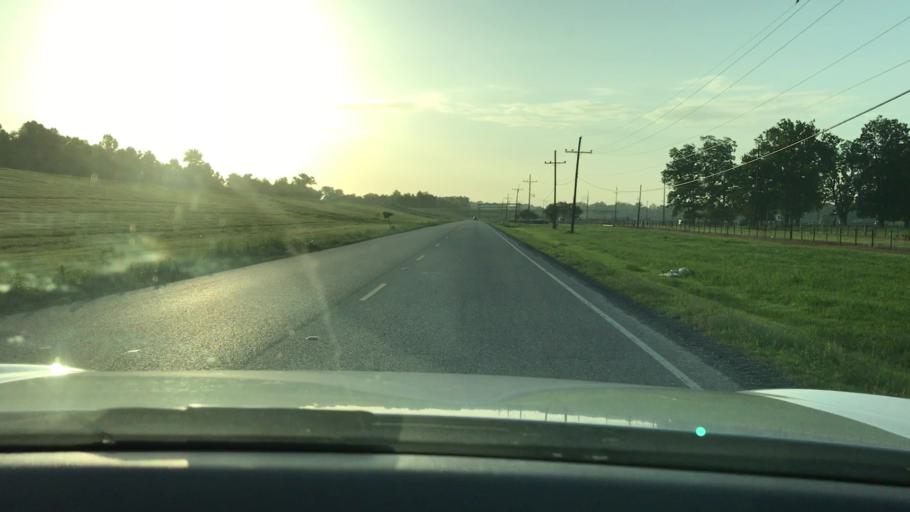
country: US
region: Louisiana
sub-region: Iberville Parish
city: Plaquemine
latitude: 30.2733
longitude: -91.1773
